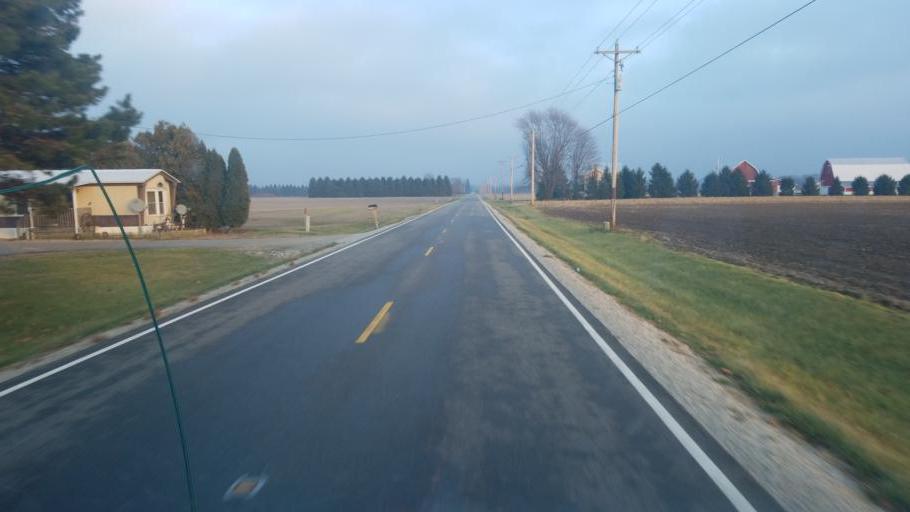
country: US
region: Ohio
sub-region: Wyandot County
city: Carey
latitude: 40.9998
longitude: -83.3015
